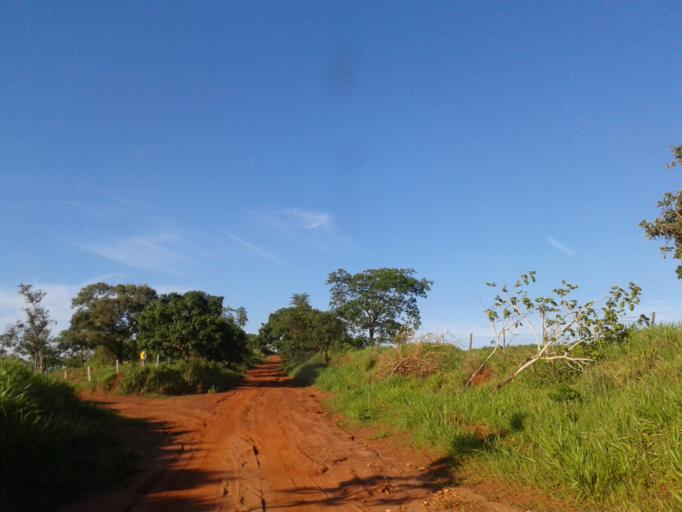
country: BR
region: Minas Gerais
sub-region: Santa Vitoria
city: Santa Vitoria
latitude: -18.9651
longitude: -49.8747
